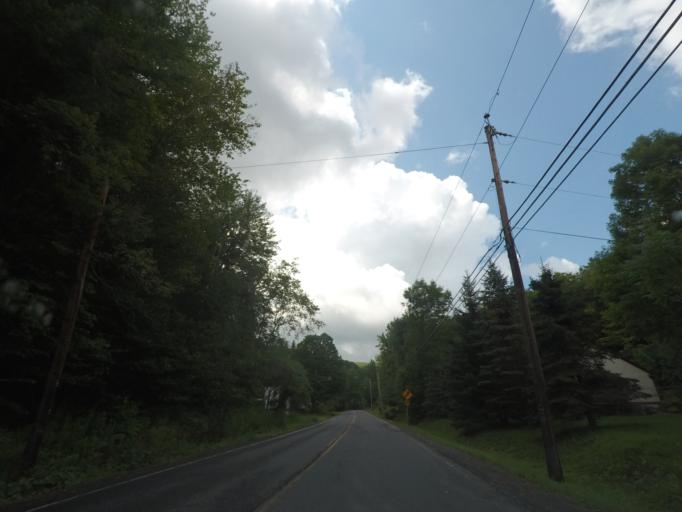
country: US
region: Massachusetts
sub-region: Berkshire County
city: Williamstown
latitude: 42.6879
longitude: -73.3813
